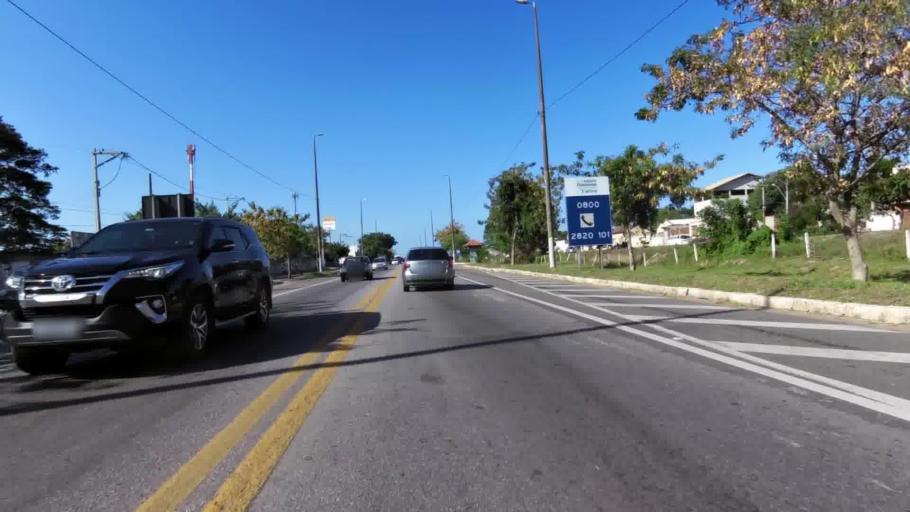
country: BR
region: Rio de Janeiro
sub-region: Campos Dos Goytacazes
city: Campos
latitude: -21.7223
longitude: -41.3172
